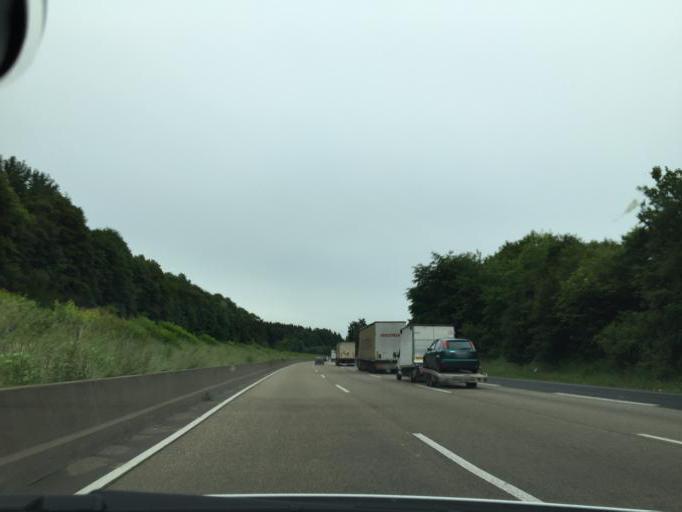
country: DE
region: Bavaria
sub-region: Regierungsbezirk Unterfranken
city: Motten
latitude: 50.3866
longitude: 9.7340
